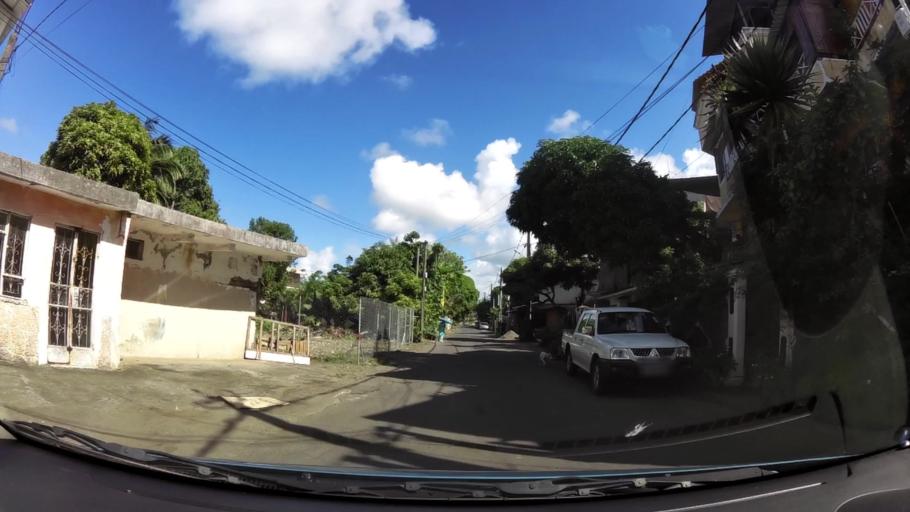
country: MU
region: Grand Port
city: Plaine Magnien
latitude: -20.4301
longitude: 57.6686
